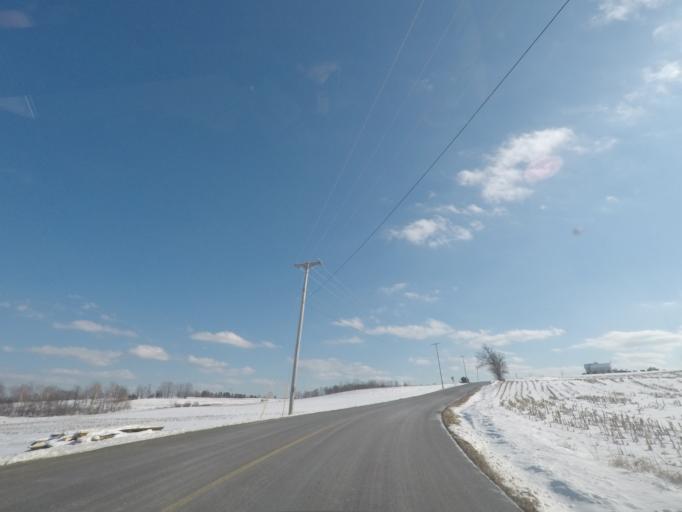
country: US
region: New York
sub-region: Rensselaer County
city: Hoosick Falls
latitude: 42.8700
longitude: -73.4925
